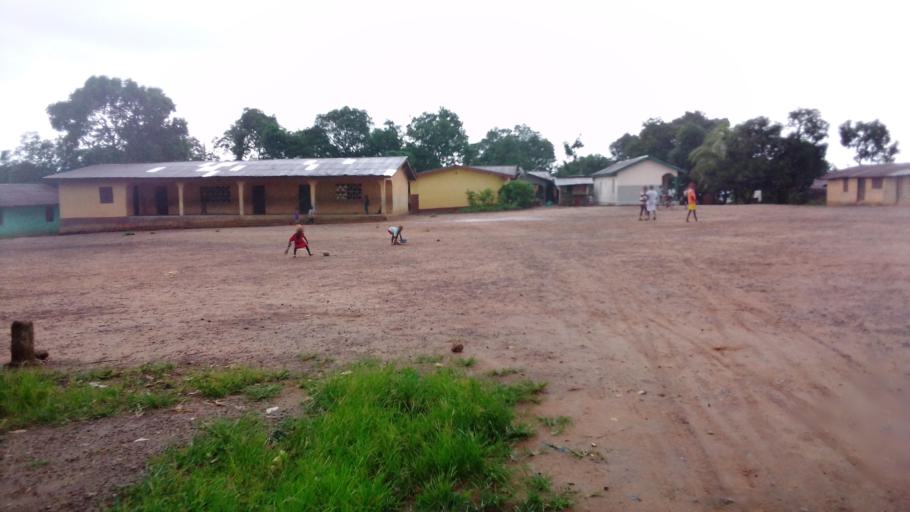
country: SL
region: Eastern Province
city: Kenema
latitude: 7.8615
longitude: -11.1748
